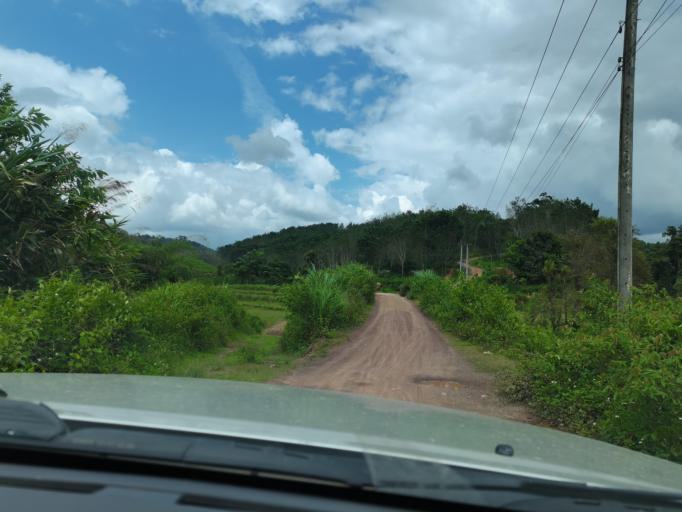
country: LA
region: Loungnamtha
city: Muang Long
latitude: 20.7007
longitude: 101.0198
